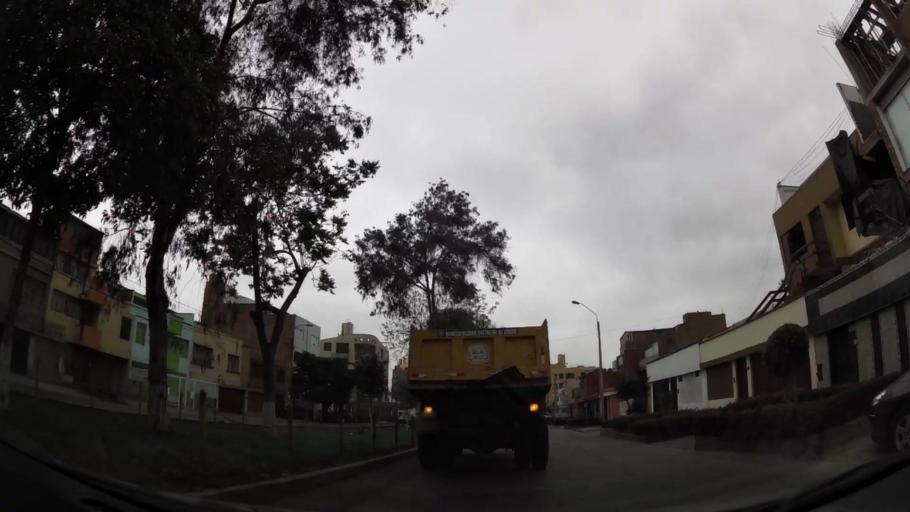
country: PE
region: Lima
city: Lima
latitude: -12.0669
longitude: -77.0576
